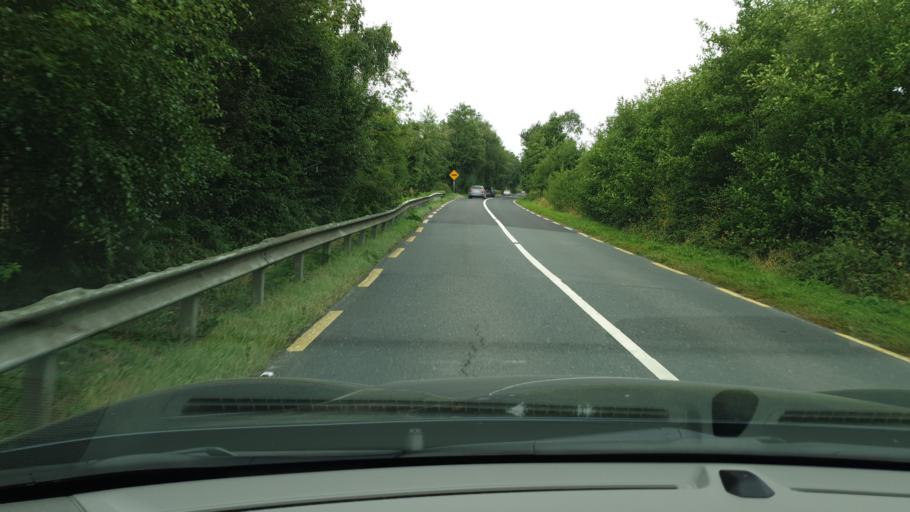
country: IE
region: Leinster
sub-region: An Mhi
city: Trim
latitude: 53.6351
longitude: -6.8195
